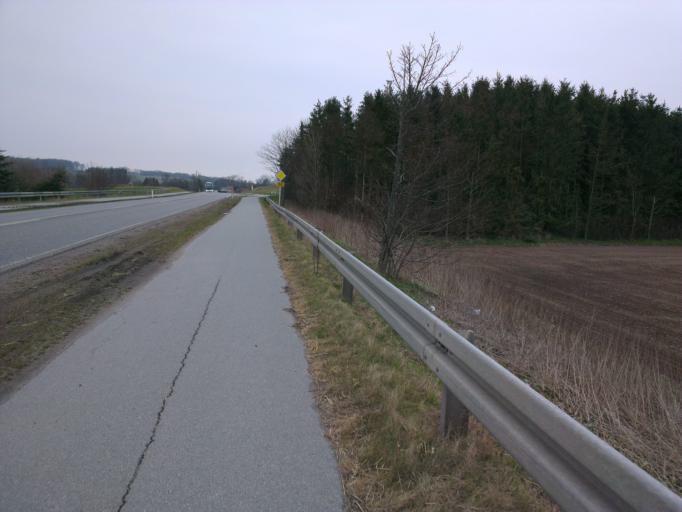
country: DK
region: Capital Region
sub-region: Frederikssund Kommune
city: Skibby
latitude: 55.7676
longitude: 11.9591
